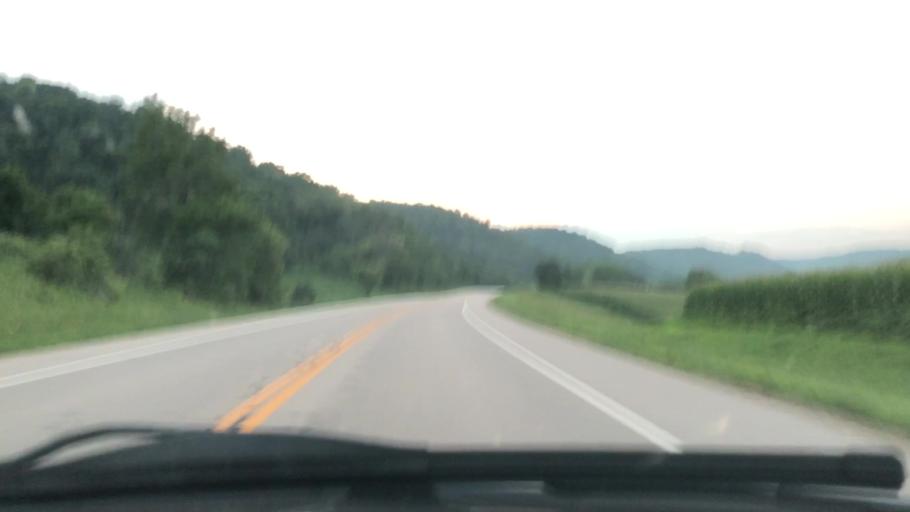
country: US
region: Wisconsin
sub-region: Richland County
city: Richland Center
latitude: 43.3511
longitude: -90.5499
